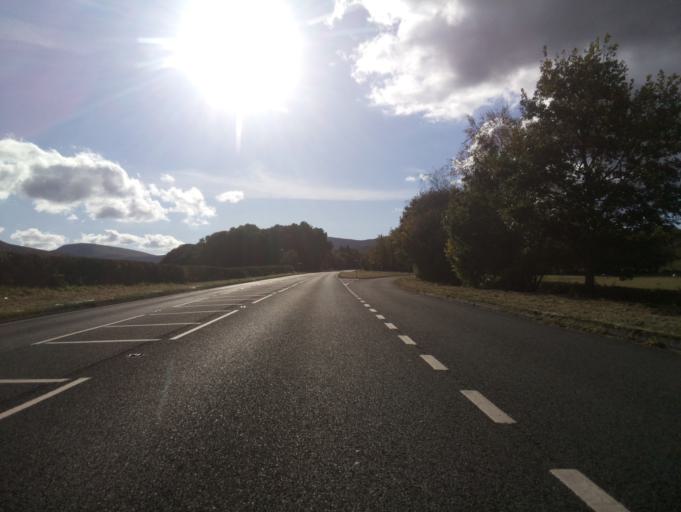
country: GB
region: Wales
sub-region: Sir Powys
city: Brecon
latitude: 51.9132
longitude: -3.4721
